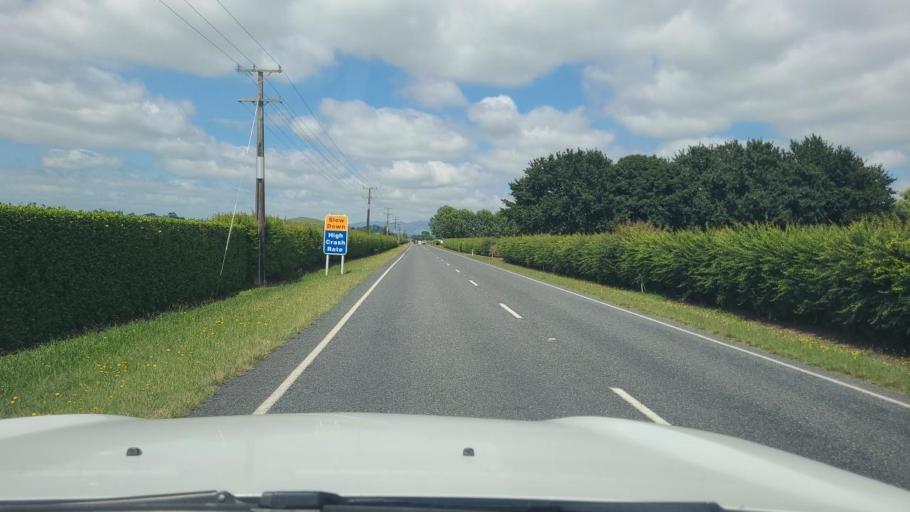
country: NZ
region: Waikato
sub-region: Matamata-Piako District
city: Matamata
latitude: -37.8771
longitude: 175.7392
